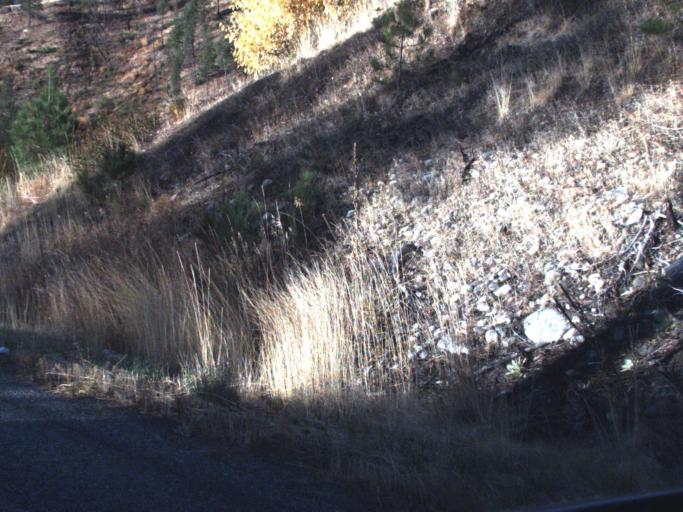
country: US
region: Washington
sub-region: Okanogan County
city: Coulee Dam
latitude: 48.0884
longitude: -118.6927
